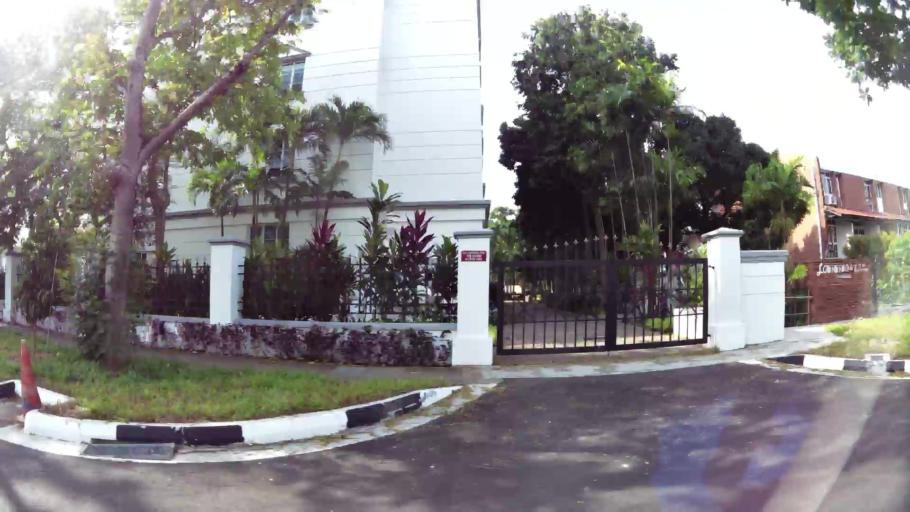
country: SG
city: Singapore
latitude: 1.2912
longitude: 103.7716
